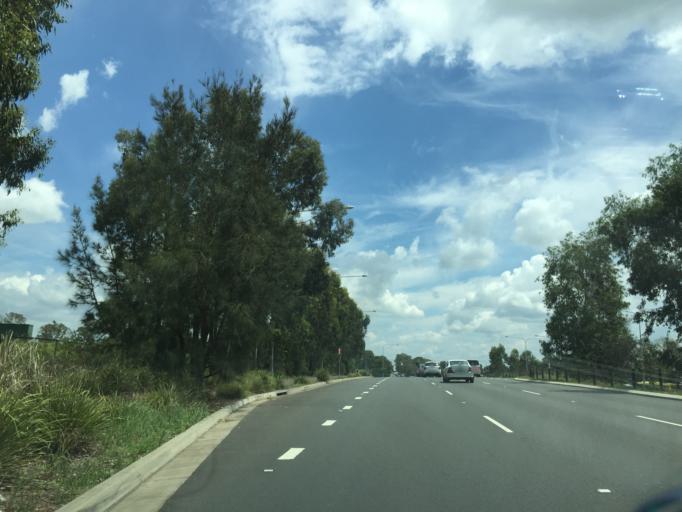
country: AU
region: New South Wales
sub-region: Blacktown
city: Rouse Hill
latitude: -33.6924
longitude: 150.9238
